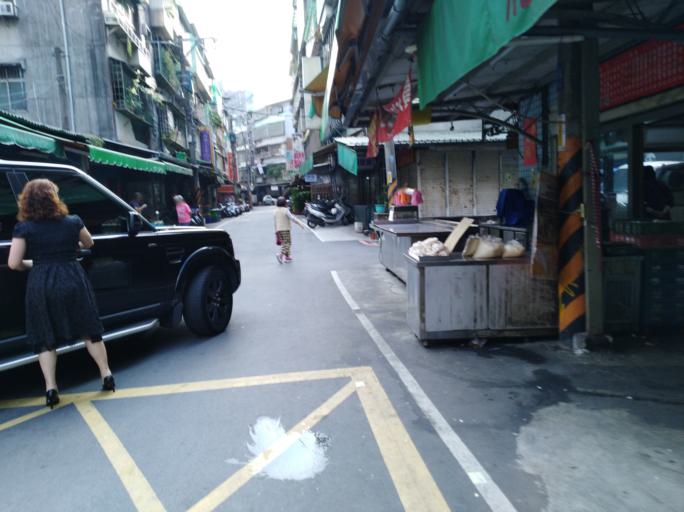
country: TW
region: Taipei
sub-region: Taipei
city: Banqiao
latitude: 25.0441
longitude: 121.4260
